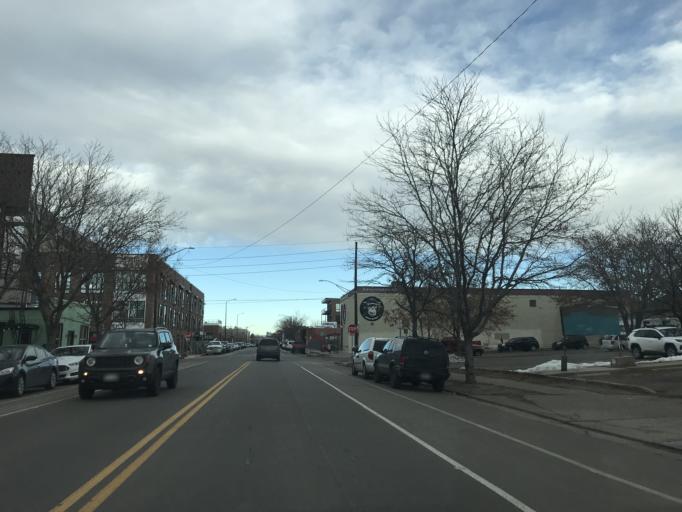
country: US
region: Colorado
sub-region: Denver County
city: Denver
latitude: 39.7637
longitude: -104.9786
